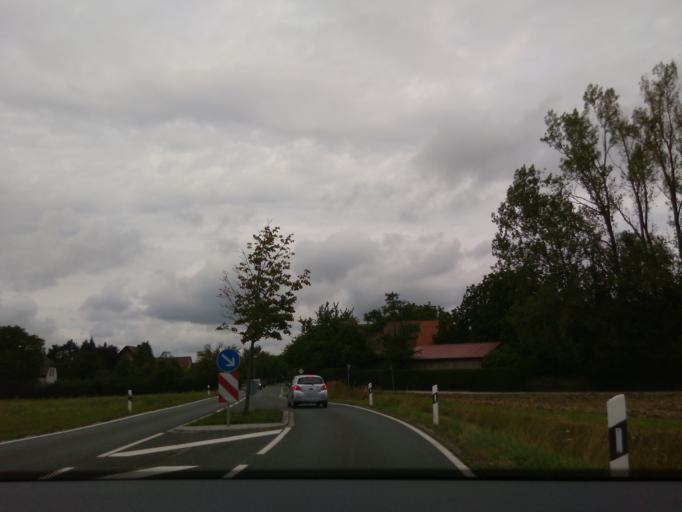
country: DE
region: Bavaria
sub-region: Regierungsbezirk Mittelfranken
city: Weisendorf
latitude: 49.6319
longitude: 10.8216
